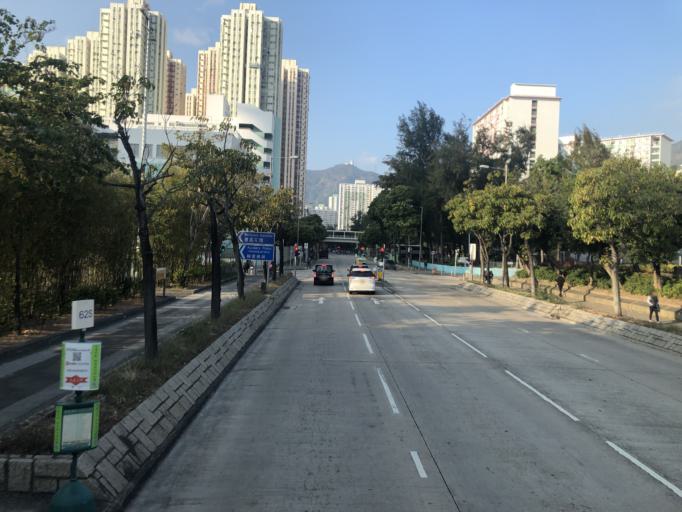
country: HK
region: Kowloon City
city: Kowloon
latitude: 22.3270
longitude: 114.2084
